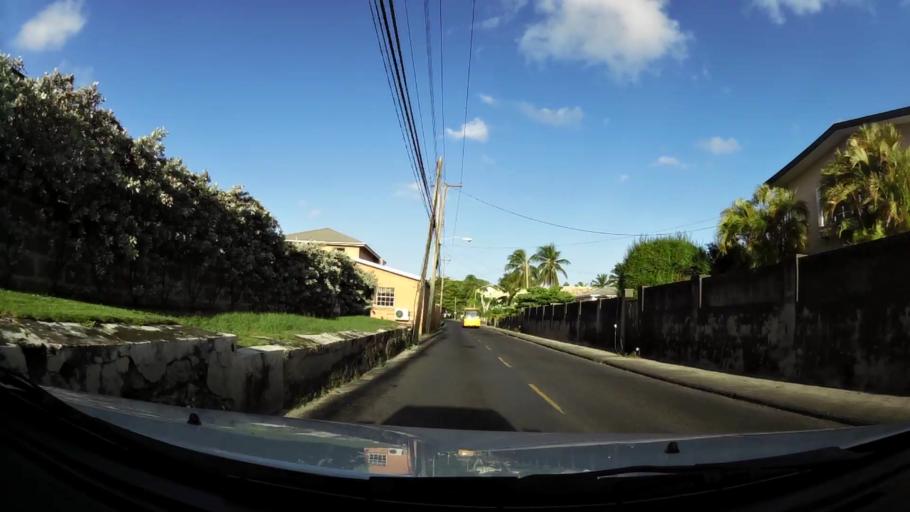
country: BB
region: Christ Church
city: Oistins
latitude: 13.0657
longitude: -59.5514
